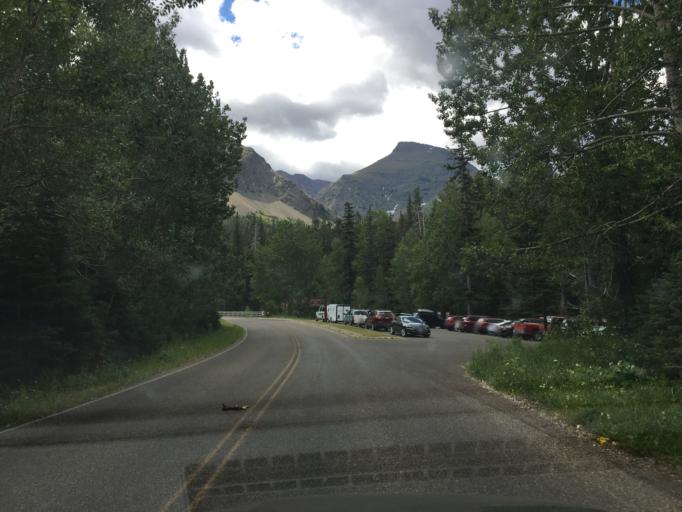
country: US
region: Montana
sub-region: Glacier County
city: South Browning
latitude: 48.4967
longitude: -113.3480
